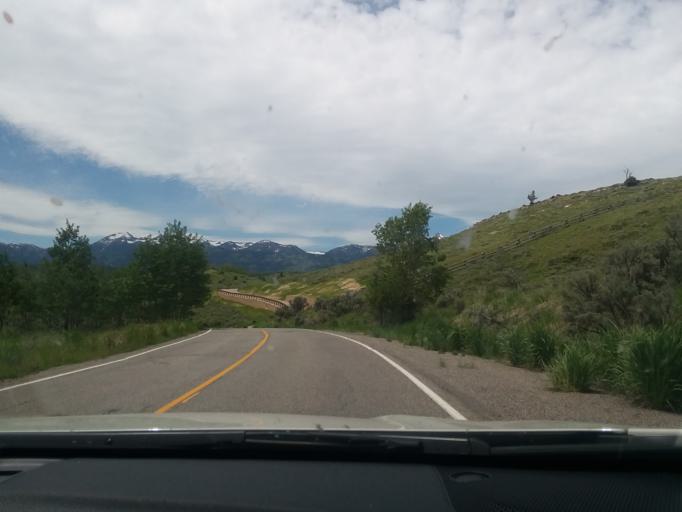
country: US
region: Wyoming
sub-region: Teton County
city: Jackson
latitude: 43.4963
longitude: -110.7756
